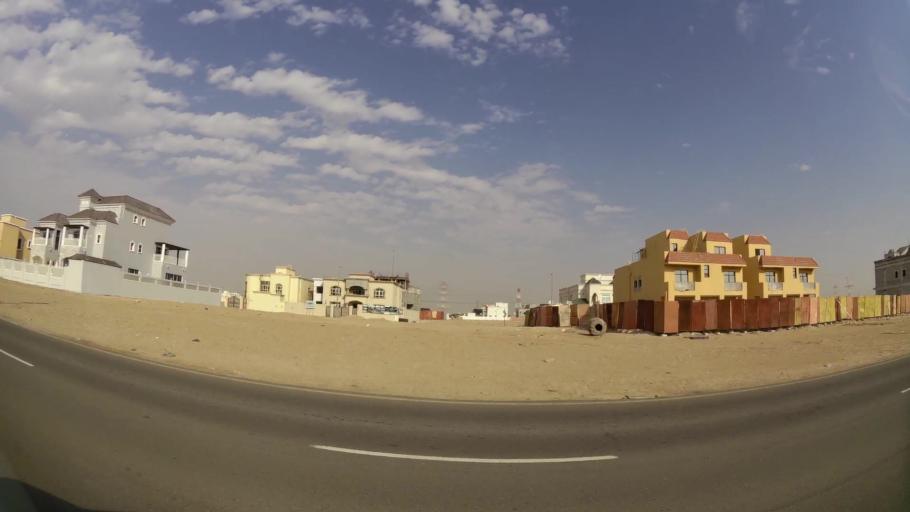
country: AE
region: Abu Dhabi
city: Abu Dhabi
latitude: 24.3287
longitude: 54.5741
